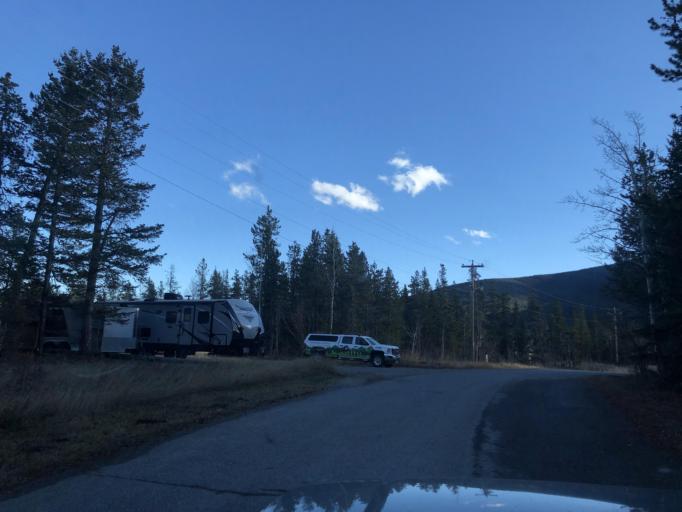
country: CA
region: Alberta
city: Canmore
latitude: 51.0727
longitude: -115.0806
